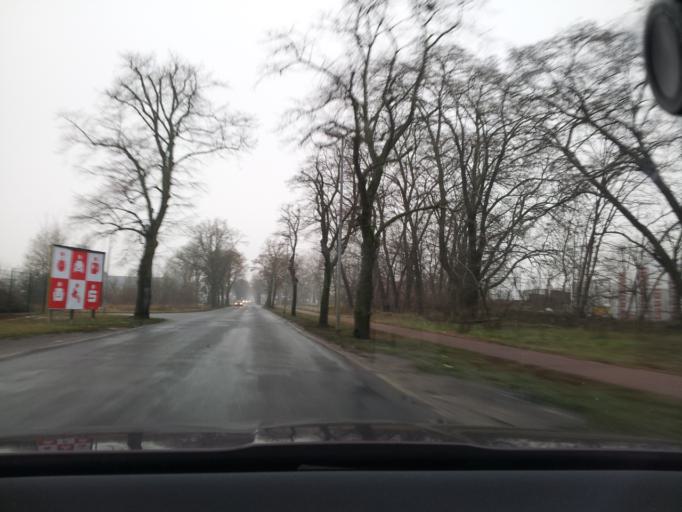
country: DE
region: Brandenburg
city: Langewahl
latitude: 52.3547
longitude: 14.0897
